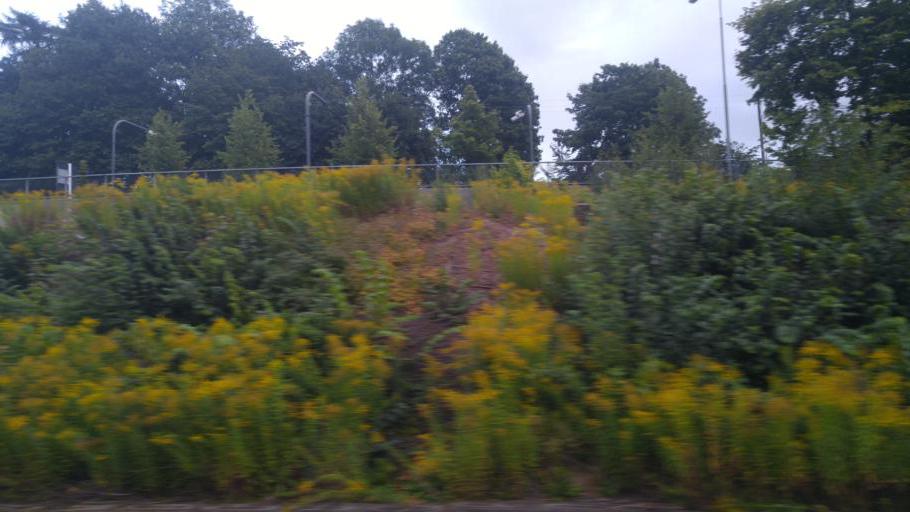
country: NO
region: Oslo
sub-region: Oslo
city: Sjolyststranda
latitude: 59.9337
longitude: 10.7092
